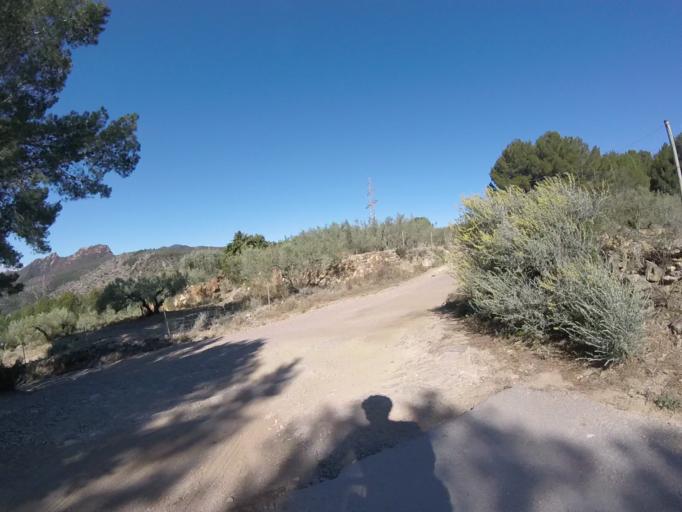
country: ES
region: Valencia
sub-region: Provincia de Castello
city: Benicassim
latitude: 40.0817
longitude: 0.0851
